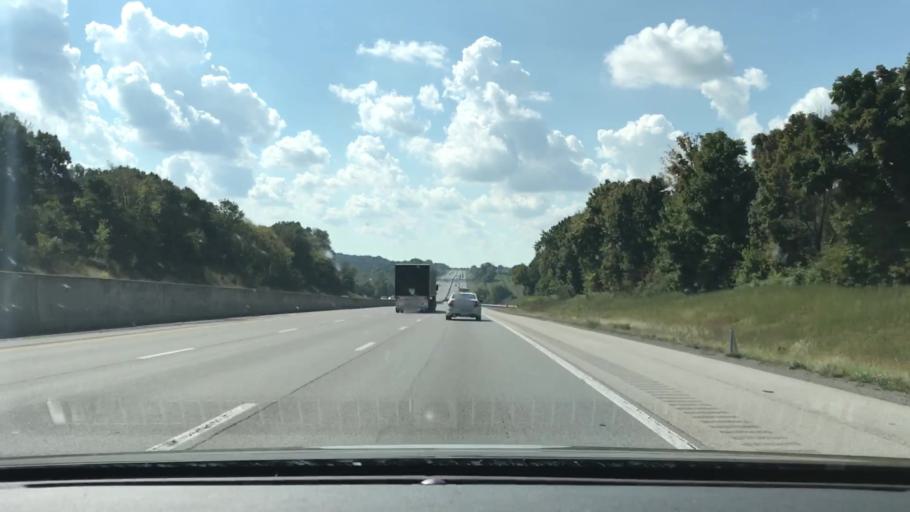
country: US
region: Kentucky
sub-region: Warren County
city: Plano
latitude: 36.8144
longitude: -86.4735
